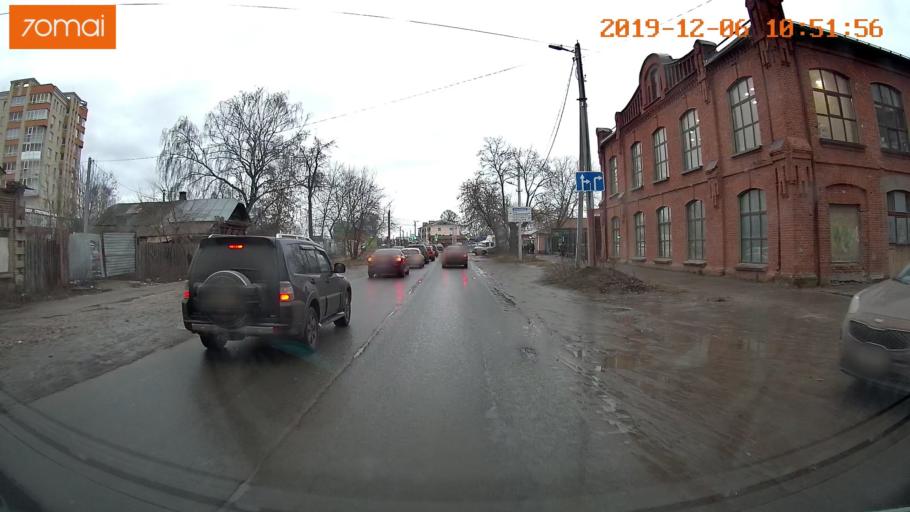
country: RU
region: Ivanovo
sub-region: Gorod Ivanovo
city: Ivanovo
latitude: 56.9863
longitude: 40.9803
